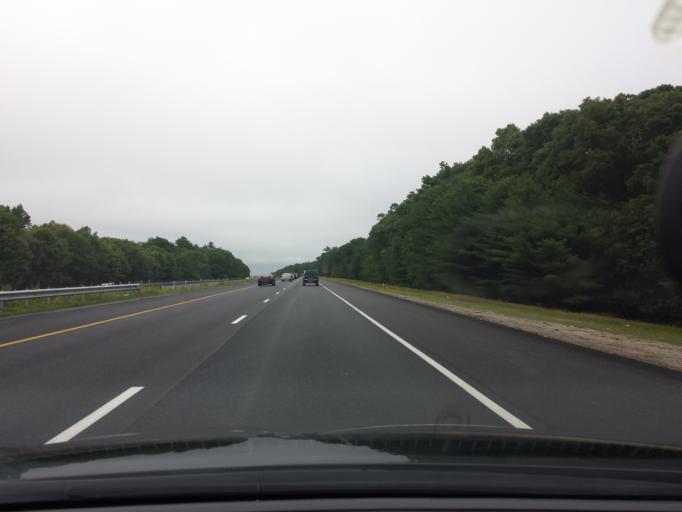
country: US
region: Rhode Island
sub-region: Kent County
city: West Greenwich
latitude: 41.5790
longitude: -71.6604
